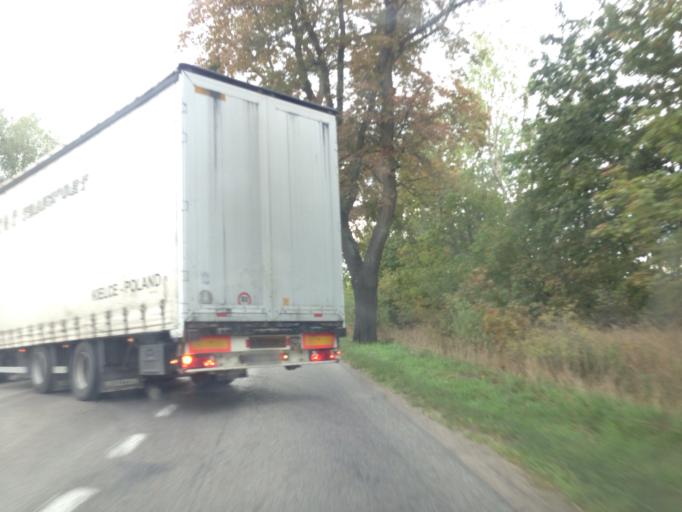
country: PL
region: Pomeranian Voivodeship
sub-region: Powiat kwidzynski
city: Kwidzyn
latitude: 53.7299
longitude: 18.9668
